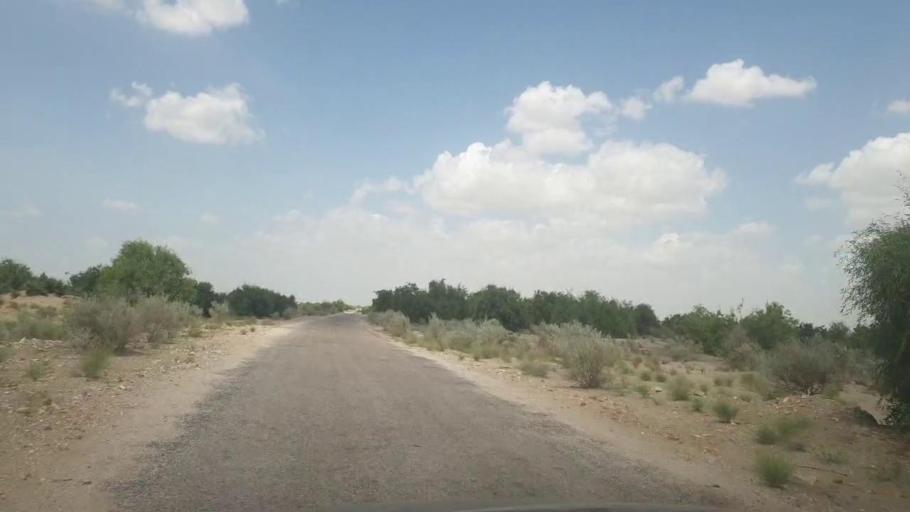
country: PK
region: Sindh
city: Kot Diji
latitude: 27.2269
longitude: 69.1133
